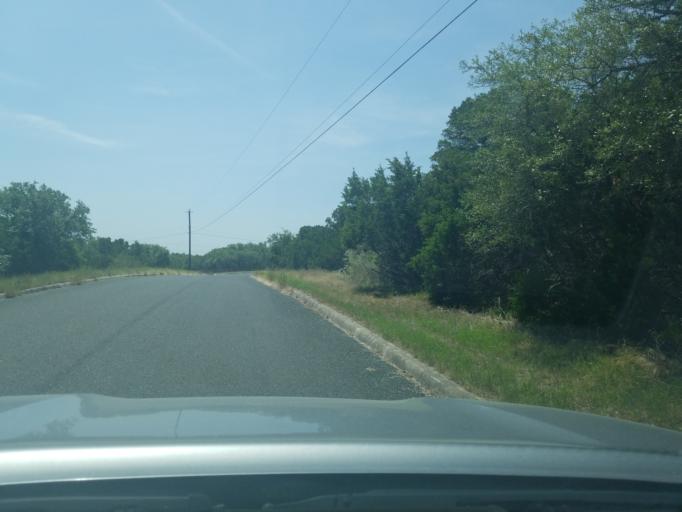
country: US
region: Texas
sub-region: Bexar County
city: Timberwood Park
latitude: 29.6756
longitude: -98.5016
